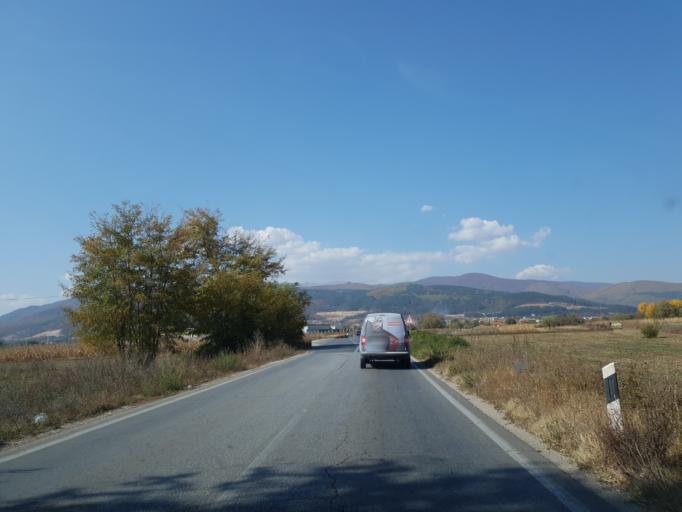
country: MK
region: Kicevo
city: Kicevo
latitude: 41.4886
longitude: 20.9705
